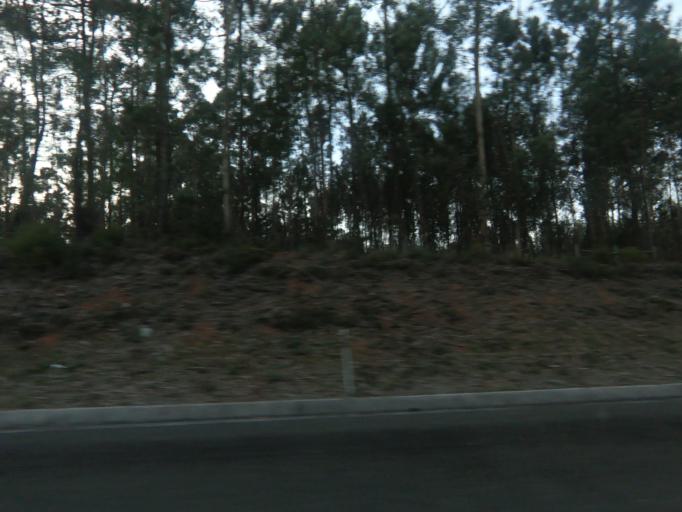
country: PT
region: Leiria
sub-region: Leiria
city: Santa Catarina da Serra
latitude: 39.6467
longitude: -8.6970
